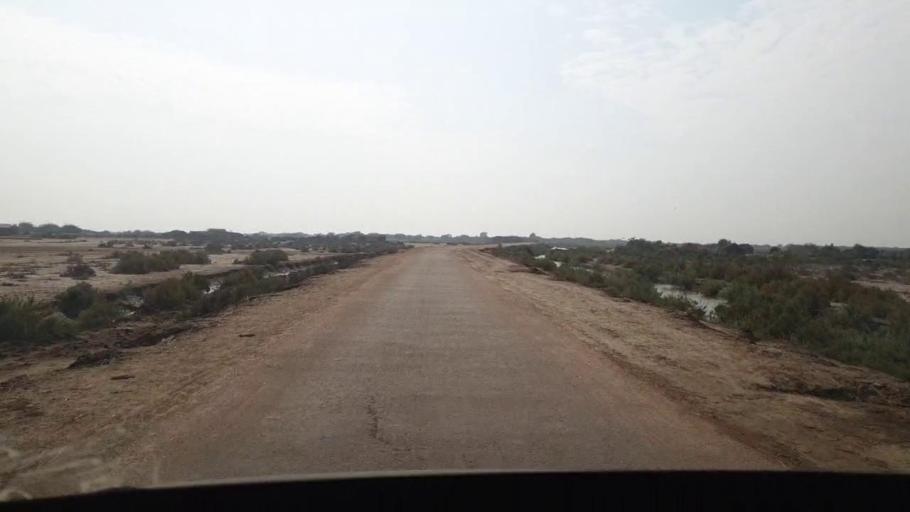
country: PK
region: Sindh
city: Chuhar Jamali
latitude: 24.2441
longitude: 67.9903
